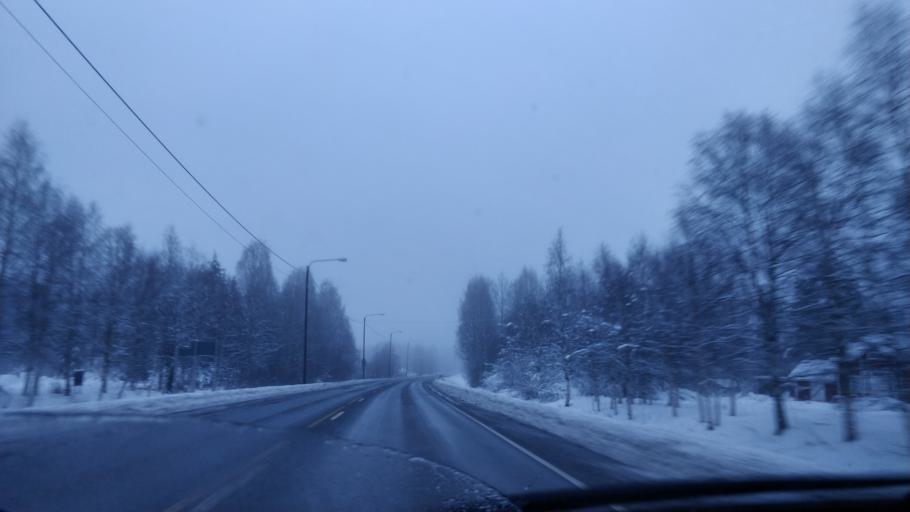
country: FI
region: Lapland
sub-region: Kemi-Tornio
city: Tervola
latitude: 66.1527
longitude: 24.9977
